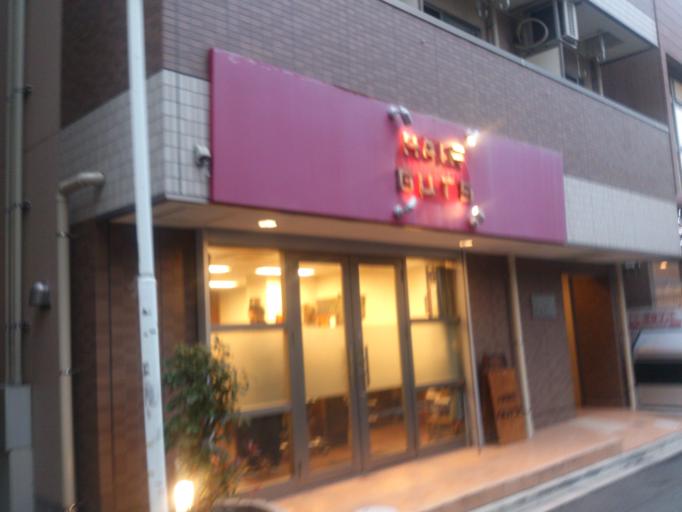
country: JP
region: Chiba
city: Matsudo
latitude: 35.7866
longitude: 139.9003
